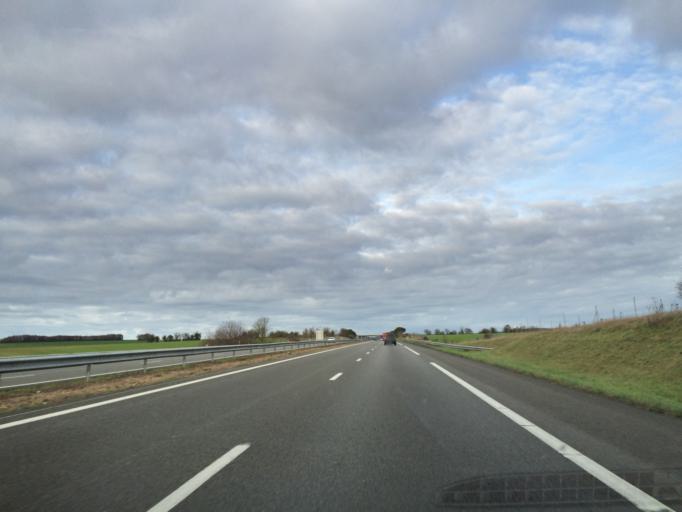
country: FR
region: Poitou-Charentes
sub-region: Departement de la Charente-Maritime
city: Saint-Jean-d'Angely
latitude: 45.9824
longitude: -0.5454
